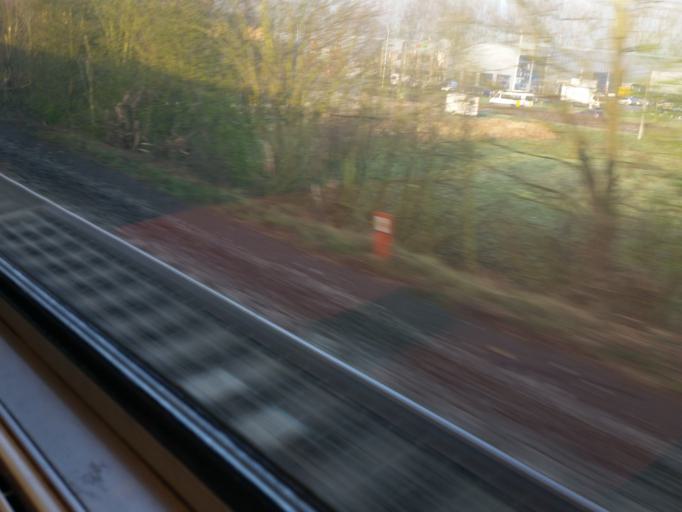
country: BE
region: Flanders
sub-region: Provincie Vlaams-Brabant
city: Zemst
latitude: 50.9553
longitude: 4.4551
